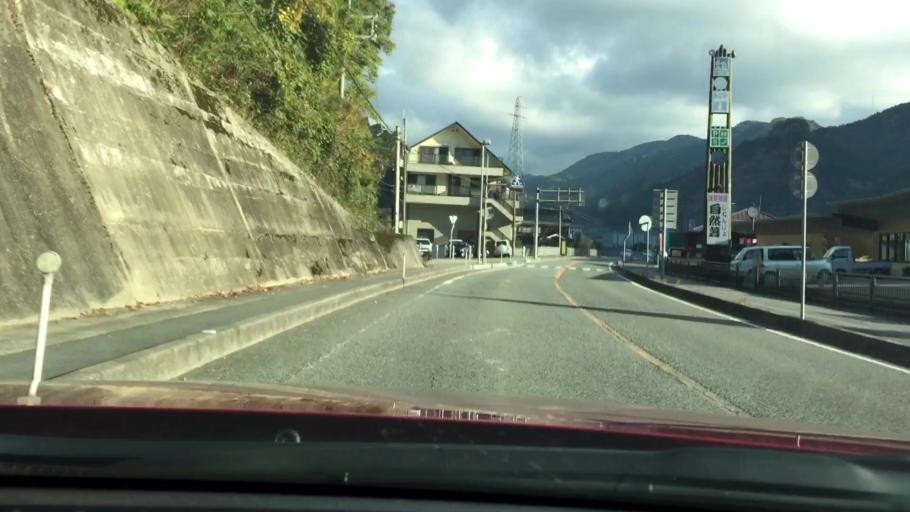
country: JP
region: Hyogo
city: Yamazakicho-nakabirose
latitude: 35.1482
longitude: 134.5394
